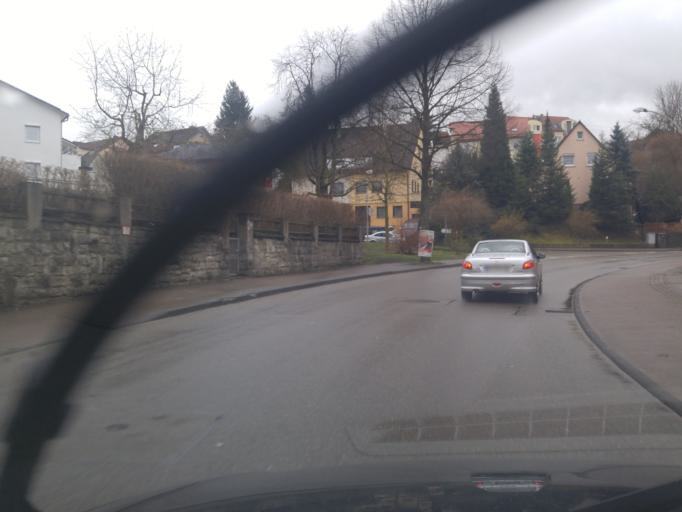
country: DE
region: Baden-Wuerttemberg
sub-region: Regierungsbezirk Stuttgart
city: Erdmannhausen
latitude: 48.9434
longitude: 9.2989
